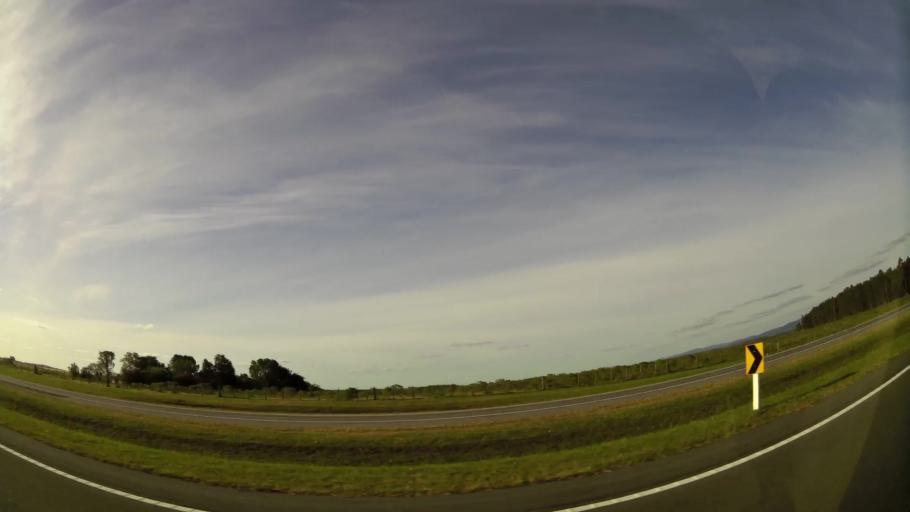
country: UY
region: Lavalleja
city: Solis de Mataojo
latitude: -34.7780
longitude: -55.4610
